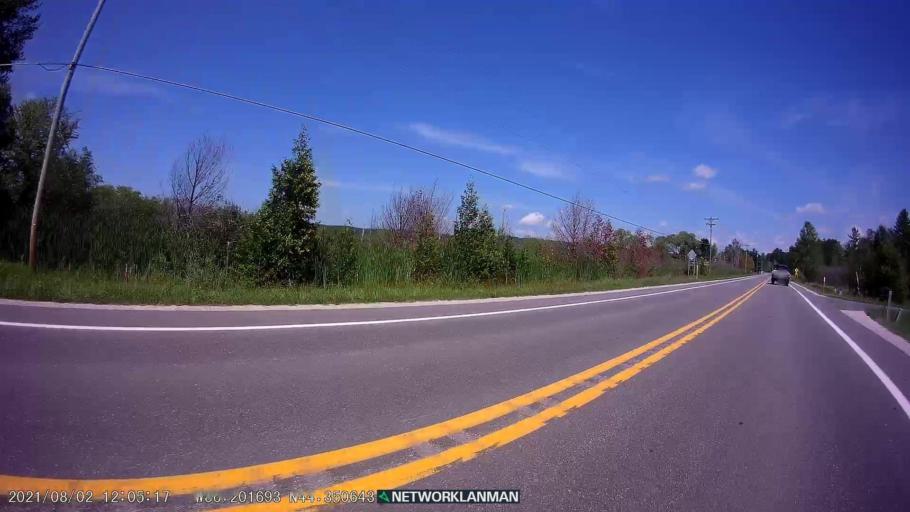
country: US
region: Michigan
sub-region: Manistee County
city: Manistee
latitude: 44.3507
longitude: -86.2013
